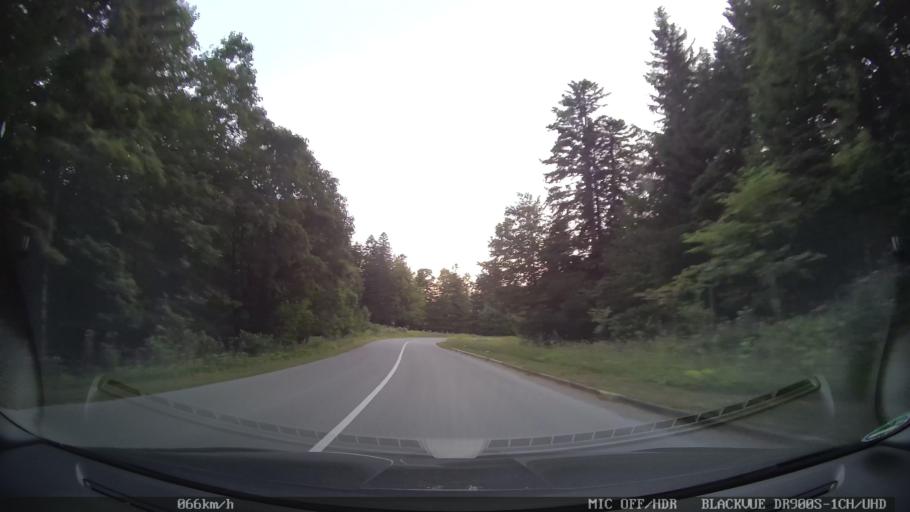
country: HR
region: Primorsko-Goranska
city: Novi Vinodolski
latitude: 45.1671
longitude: 14.9602
